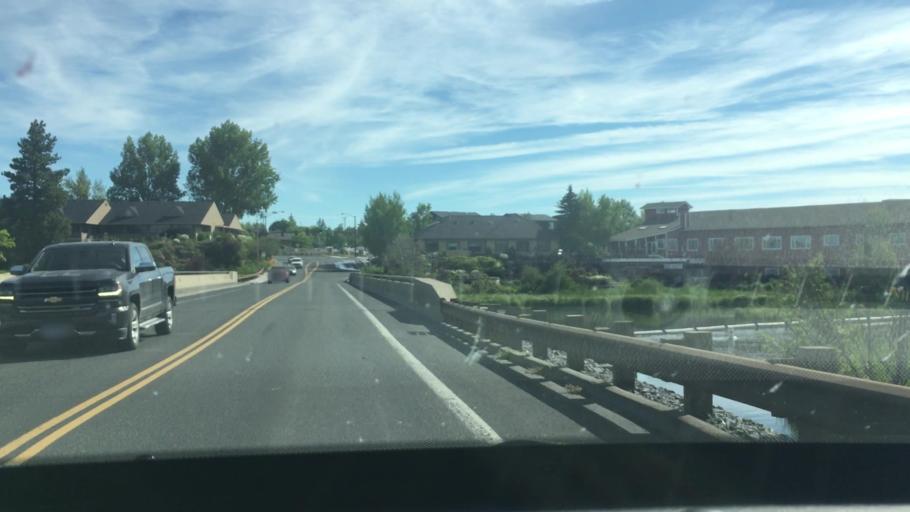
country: US
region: Oregon
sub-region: Deschutes County
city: Bend
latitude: 44.0495
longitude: -121.3210
